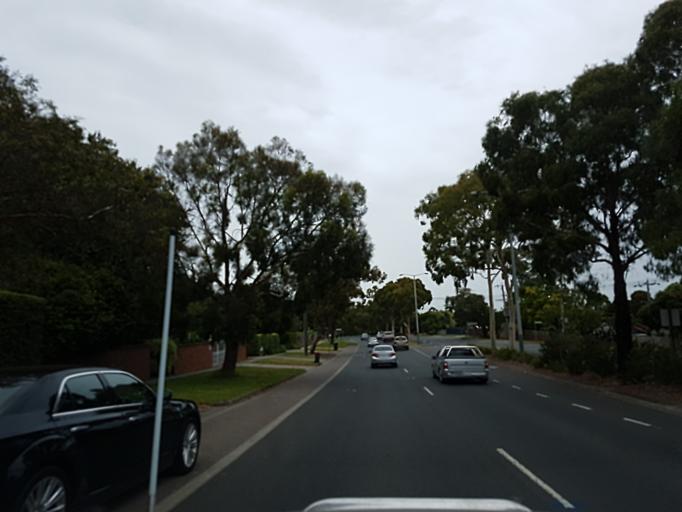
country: AU
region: Victoria
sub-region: Whitehorse
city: Vermont
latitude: -37.8376
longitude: 145.1973
